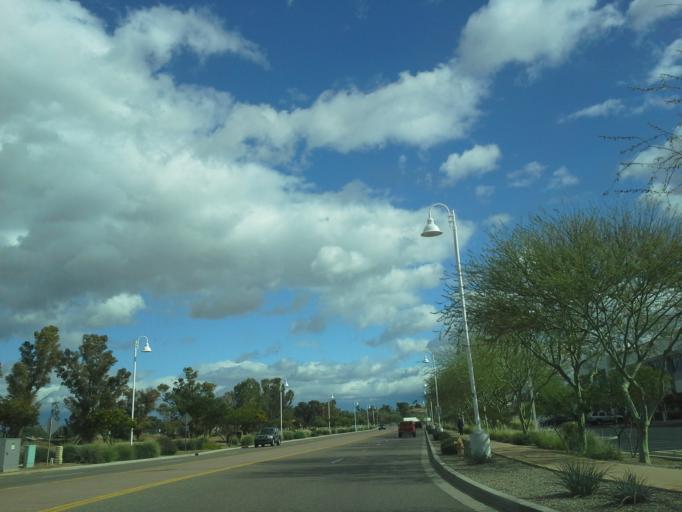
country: US
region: Arizona
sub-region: Maricopa County
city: Mesa
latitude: 33.4365
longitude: -111.8598
